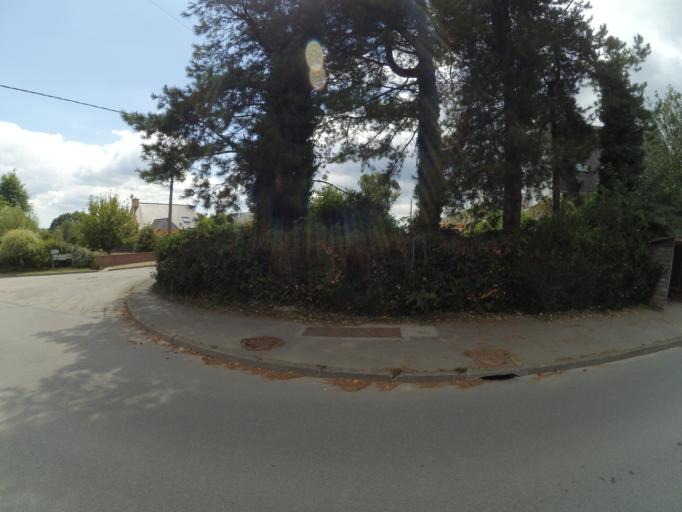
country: FR
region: Brittany
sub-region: Departement du Morbihan
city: Landaul
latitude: 47.7471
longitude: -3.0729
